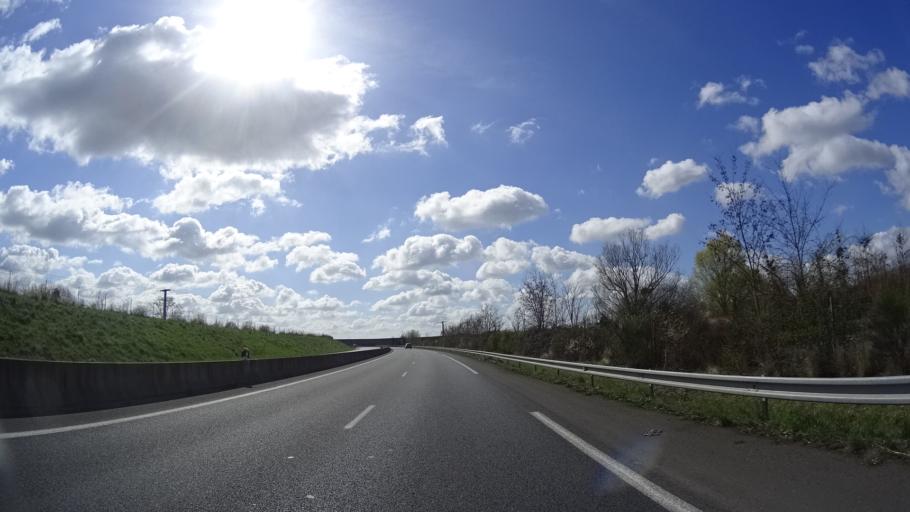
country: FR
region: Pays de la Loire
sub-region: Departement de Maine-et-Loire
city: Saint-Jean
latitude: 47.2970
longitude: -0.3894
